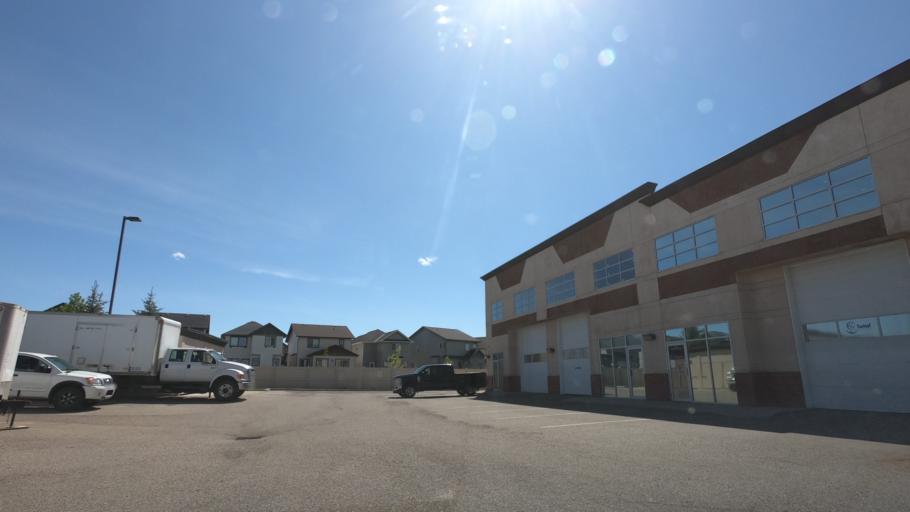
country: CA
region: Alberta
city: Airdrie
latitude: 51.2625
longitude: -113.9938
